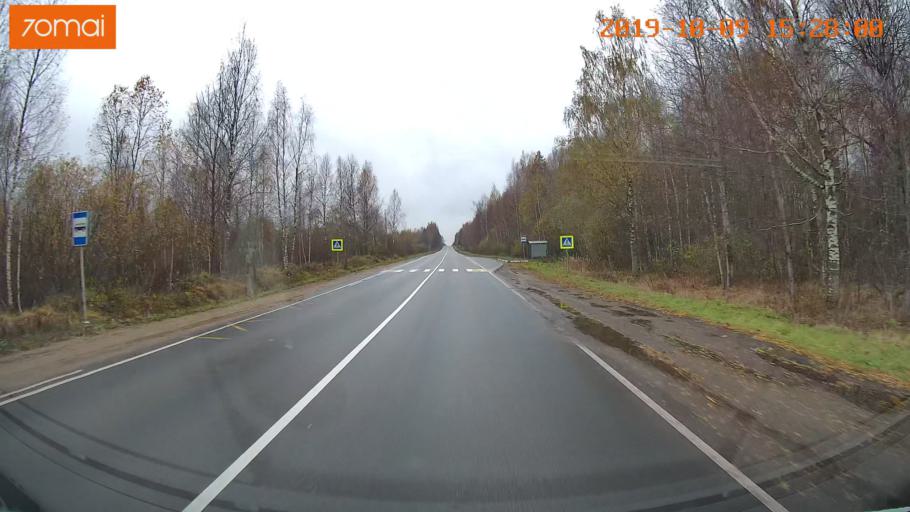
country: RU
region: Kostroma
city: Susanino
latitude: 58.0082
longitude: 41.3674
